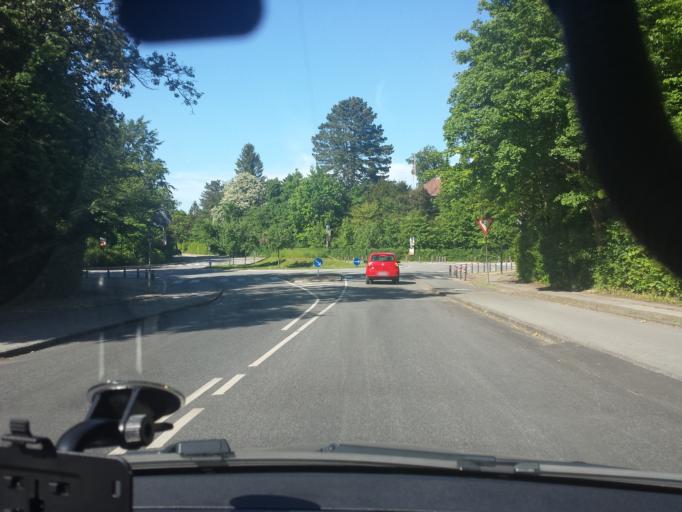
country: DK
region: Capital Region
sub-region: Gentofte Kommune
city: Charlottenlund
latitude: 55.7679
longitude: 12.5848
